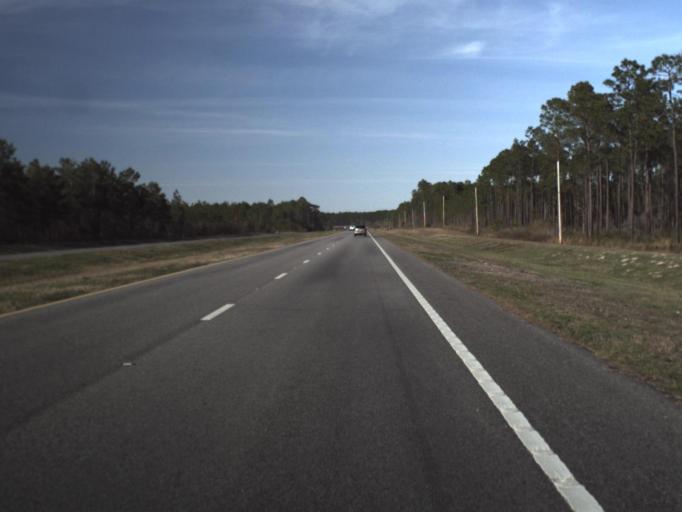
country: US
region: Florida
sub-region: Bay County
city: Laguna Beach
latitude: 30.4007
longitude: -85.8712
